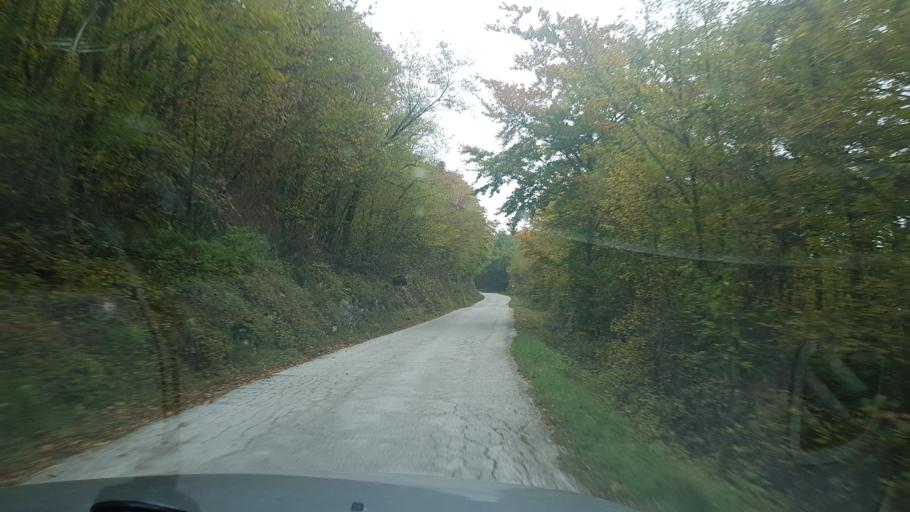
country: HR
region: Istarska
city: Buzet
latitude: 45.4590
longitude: 14.0346
